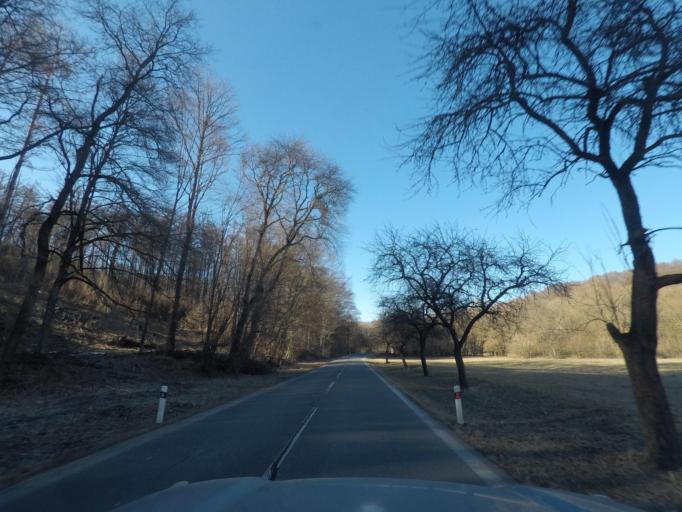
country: SK
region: Presovsky
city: Medzilaborce
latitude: 49.1713
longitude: 22.0241
